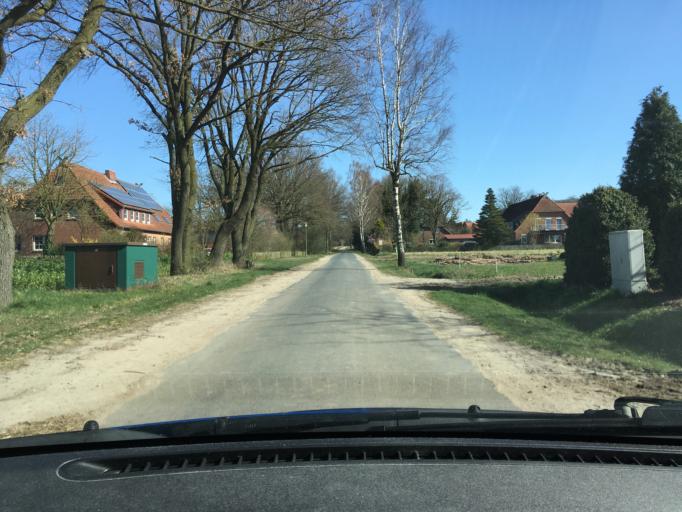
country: DE
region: Lower Saxony
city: Schwienau
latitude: 53.0249
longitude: 10.4421
